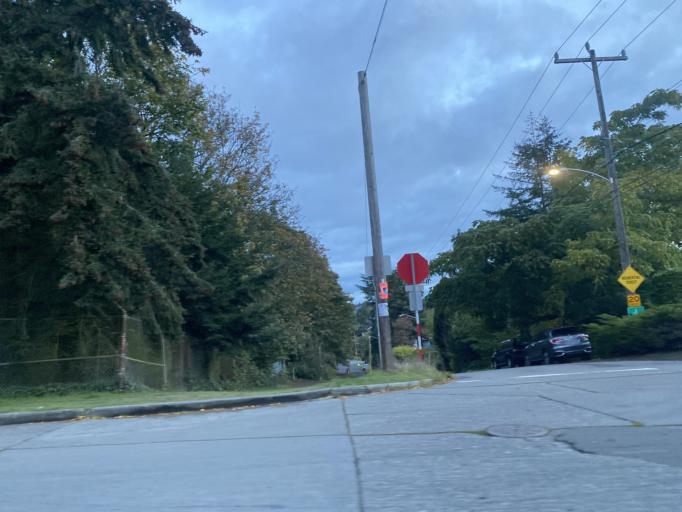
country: US
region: Washington
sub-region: King County
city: Seattle
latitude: 47.6541
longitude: -122.4037
